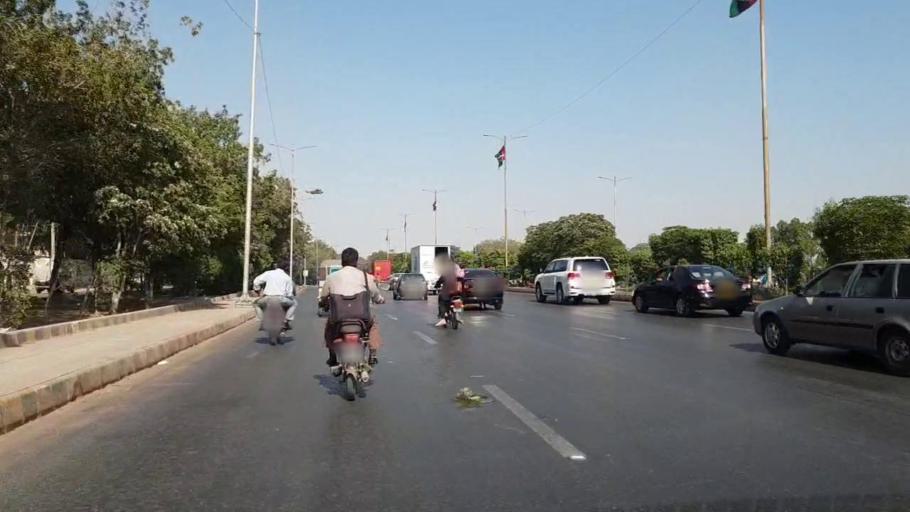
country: PK
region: Sindh
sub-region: Karachi District
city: Karachi
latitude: 24.8729
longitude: 67.0924
